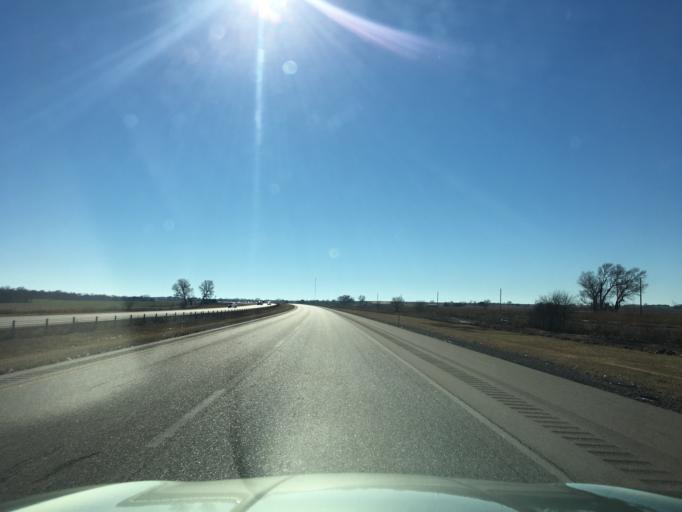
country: US
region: Oklahoma
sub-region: Kay County
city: Blackwell
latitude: 36.9028
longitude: -97.3540
